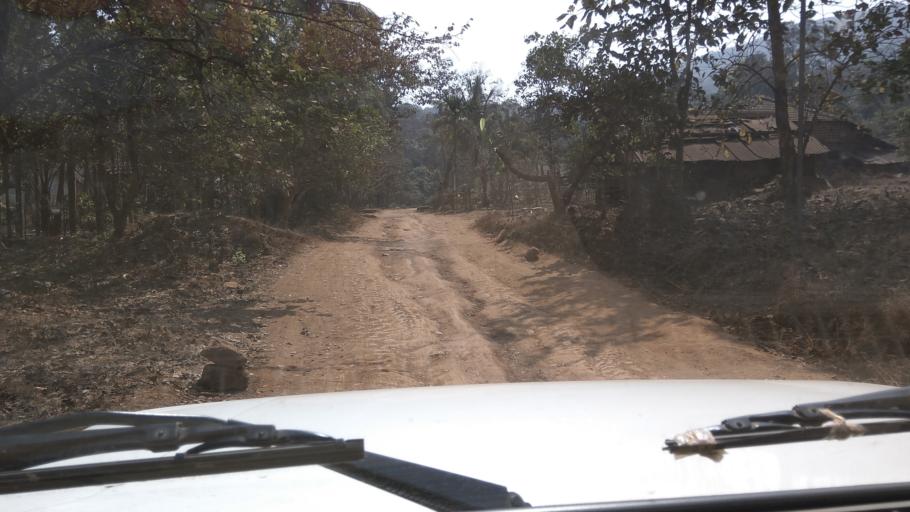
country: IN
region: Goa
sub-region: South Goa
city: Sanguem
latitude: 15.3120
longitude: 74.2966
